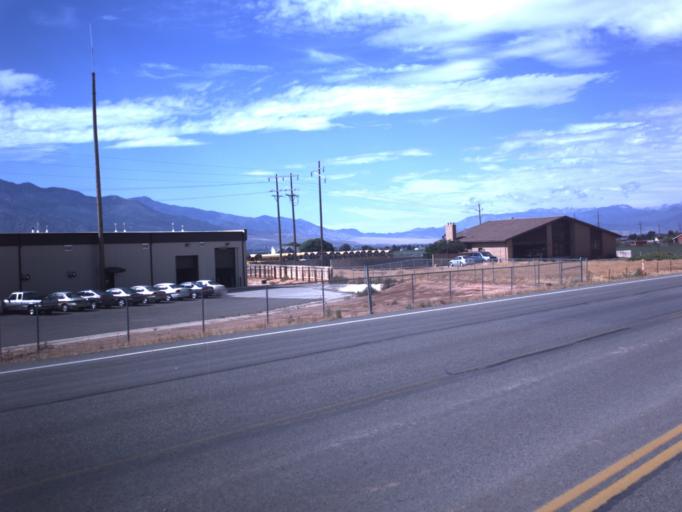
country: US
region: Utah
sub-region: Sevier County
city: Richfield
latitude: 38.7908
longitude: -112.0448
